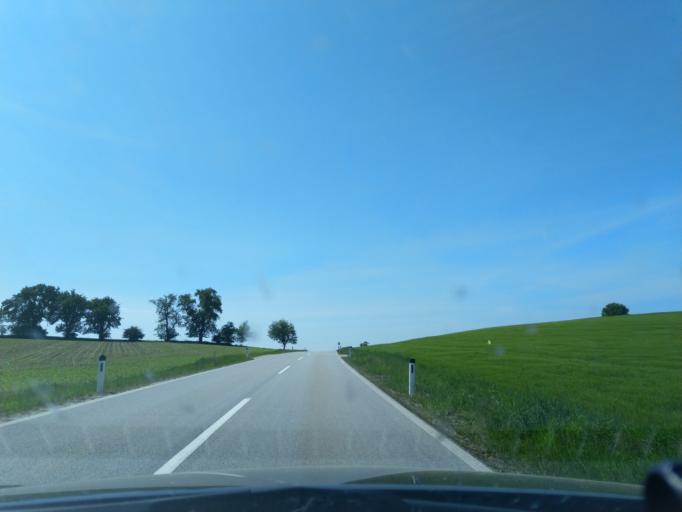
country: DE
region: Bavaria
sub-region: Lower Bavaria
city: Bad Fussing
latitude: 48.2683
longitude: 13.3447
